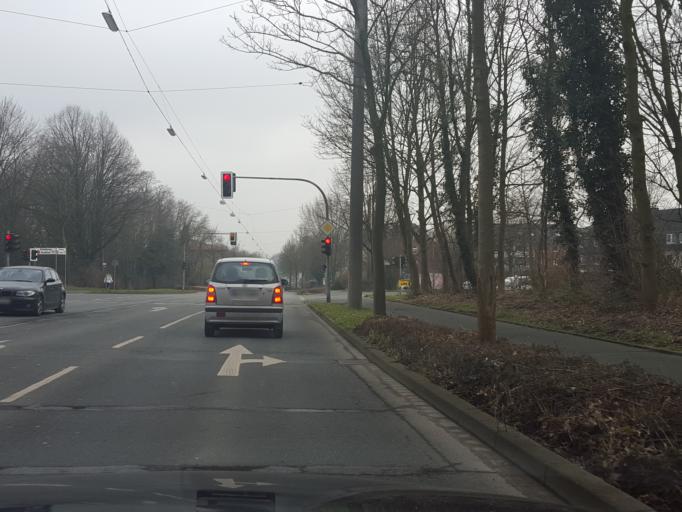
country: DE
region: North Rhine-Westphalia
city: Oer-Erkenschwick
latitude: 51.6429
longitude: 7.2482
